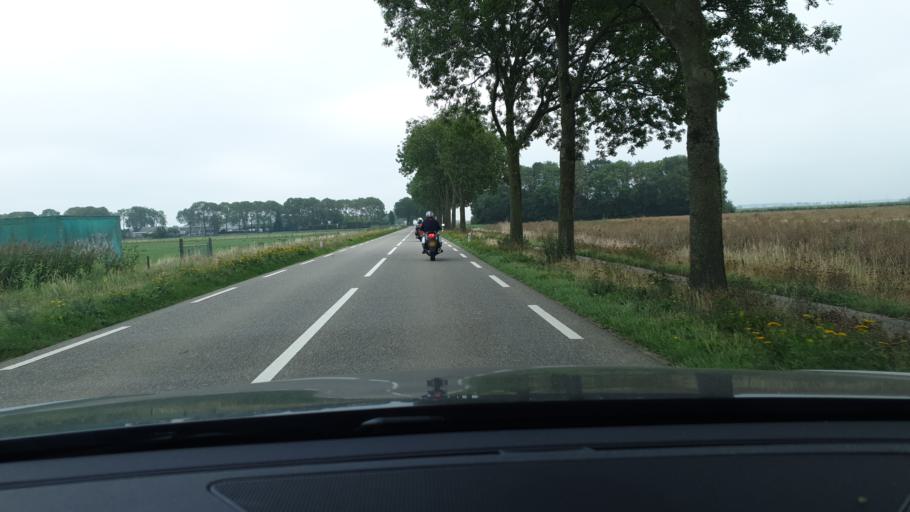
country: NL
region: North Brabant
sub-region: Gemeente 's-Hertogenbosch
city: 's-Hertogenbosch
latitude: 51.7422
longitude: 5.3518
